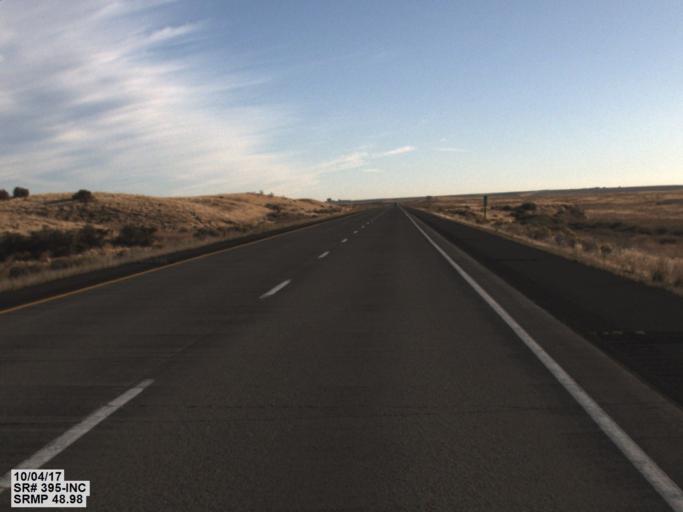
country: US
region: Washington
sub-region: Franklin County
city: Connell
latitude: 46.5964
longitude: -118.9451
